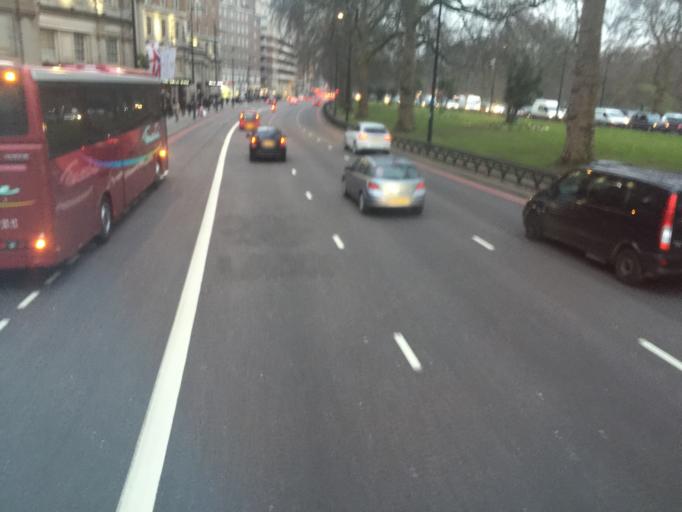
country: GB
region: England
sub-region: Greater London
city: Chelsea
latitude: 51.5099
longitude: -0.1561
